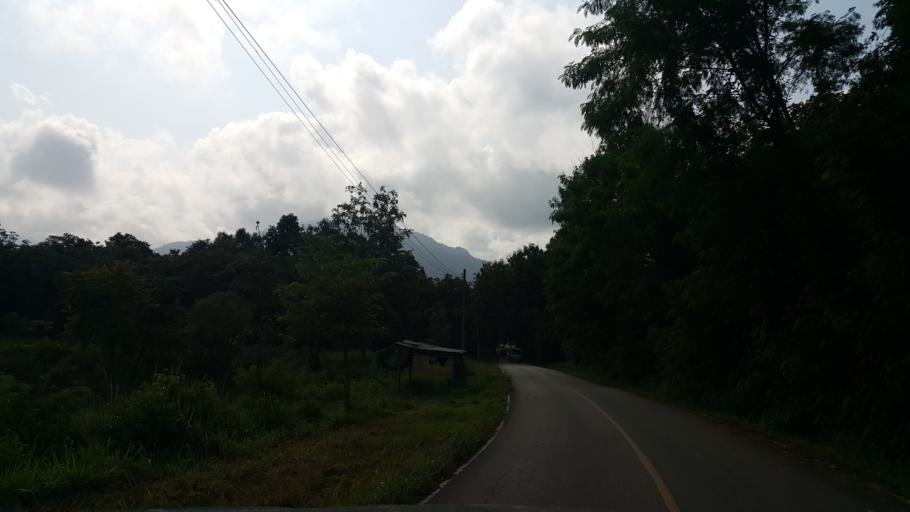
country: TH
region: Chiang Mai
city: Mae On
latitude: 18.7459
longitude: 99.2213
